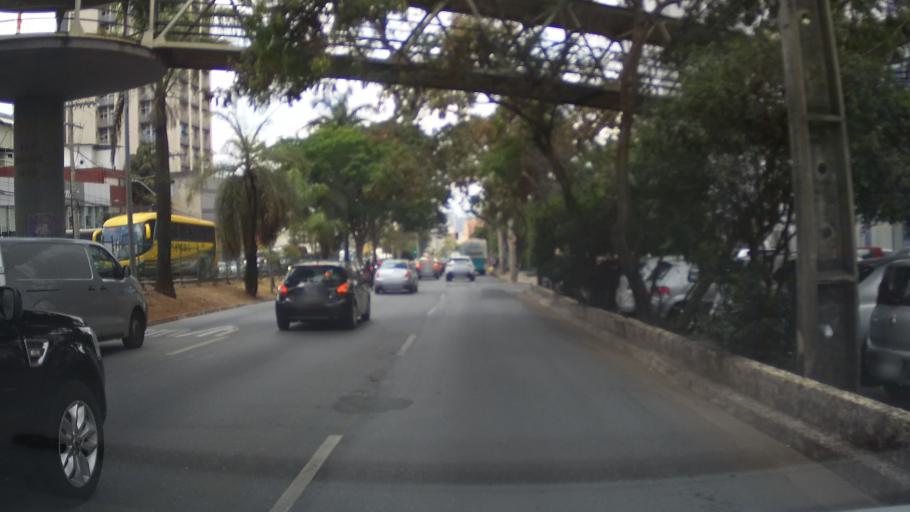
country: BR
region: Minas Gerais
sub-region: Belo Horizonte
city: Belo Horizonte
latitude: -19.9549
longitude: -43.9399
